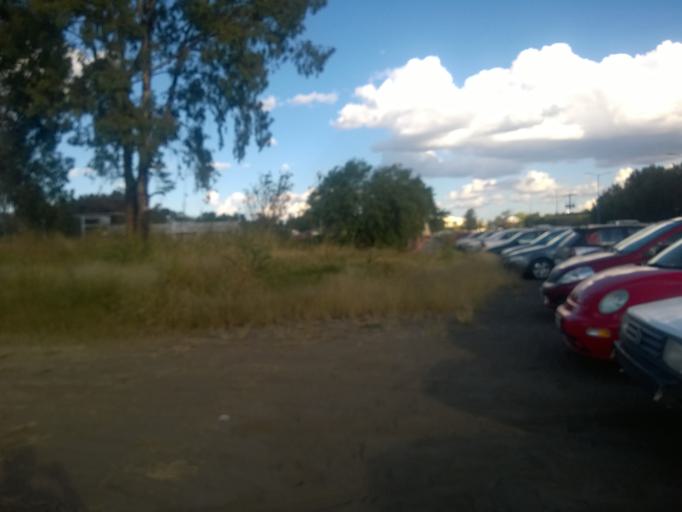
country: MX
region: Guanajuato
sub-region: Leon
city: Ladrilleras del Refugio
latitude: 21.0646
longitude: -101.5849
